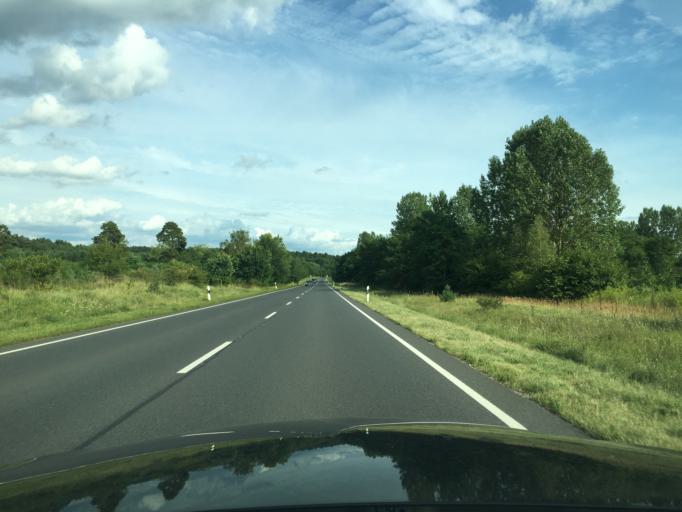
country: DE
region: Mecklenburg-Vorpommern
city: Neustrelitz
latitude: 53.3794
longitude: 13.0627
